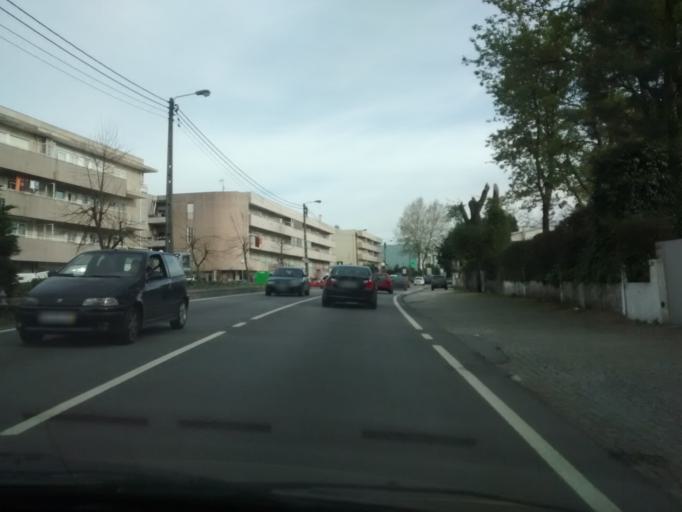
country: PT
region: Braga
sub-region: Guimaraes
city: Ponte
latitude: 41.4800
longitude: -8.3397
